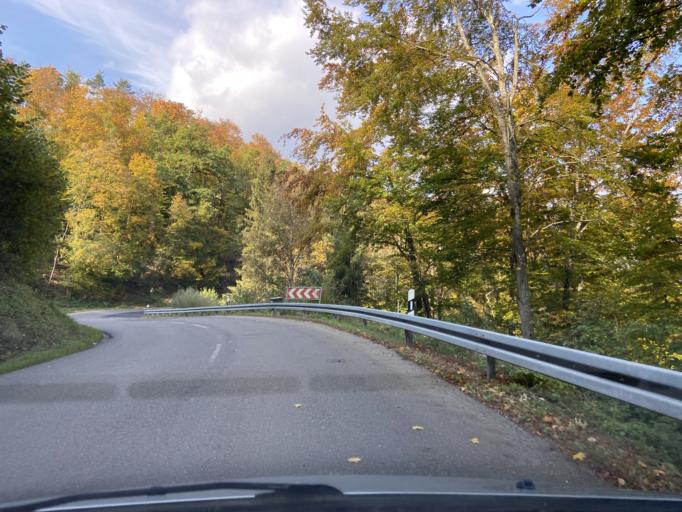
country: DE
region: Baden-Wuerttemberg
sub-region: Tuebingen Region
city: Sigmaringen
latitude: 48.0753
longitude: 9.2273
